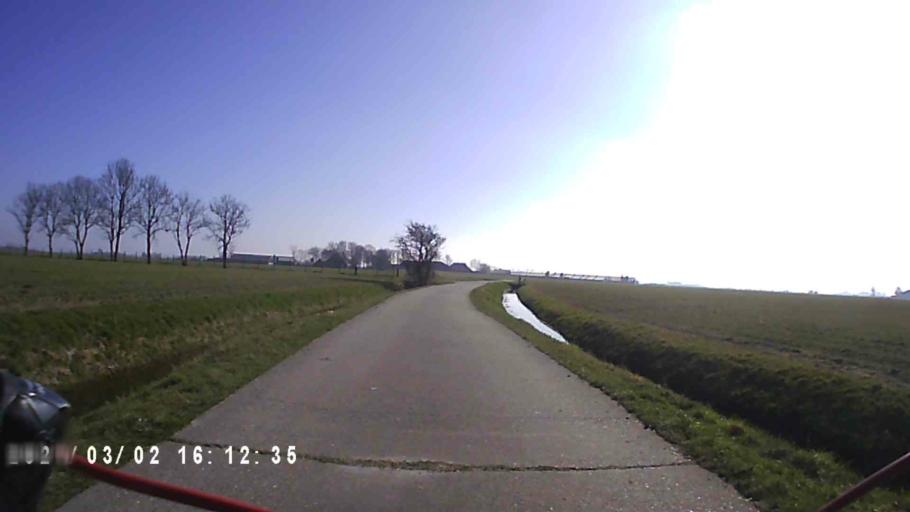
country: NL
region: Groningen
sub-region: Gemeente Zuidhorn
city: Oldehove
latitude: 53.2983
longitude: 6.3973
